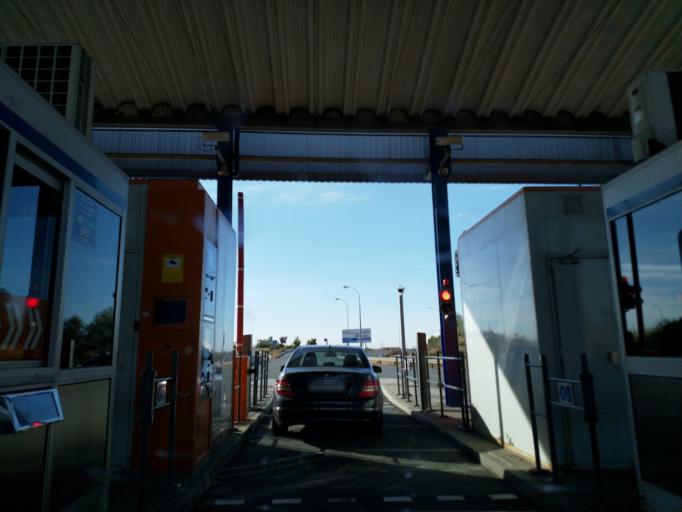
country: ES
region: Castille and Leon
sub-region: Provincia de Segovia
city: Villacastin
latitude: 40.7726
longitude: -4.4241
